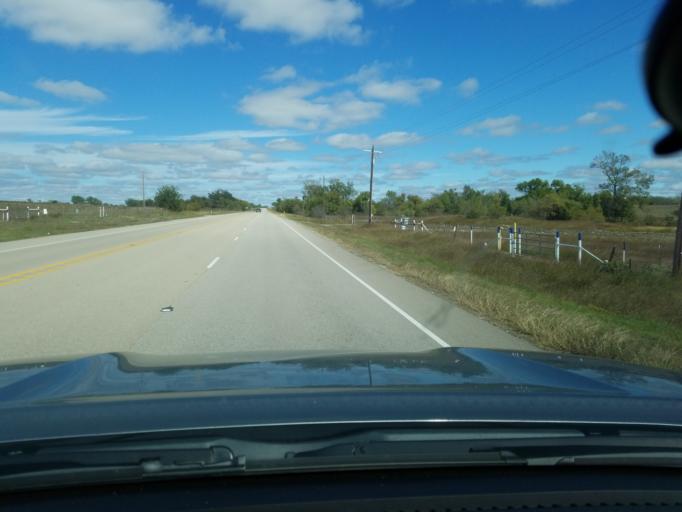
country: US
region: Texas
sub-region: Hamilton County
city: Hamilton
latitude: 31.6499
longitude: -98.1463
